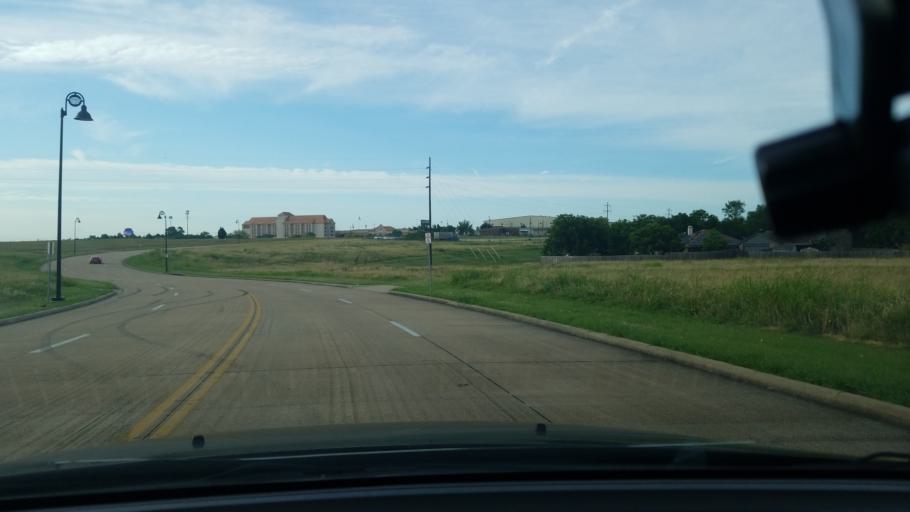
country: US
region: Texas
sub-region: Dallas County
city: Mesquite
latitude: 32.7667
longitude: -96.6277
